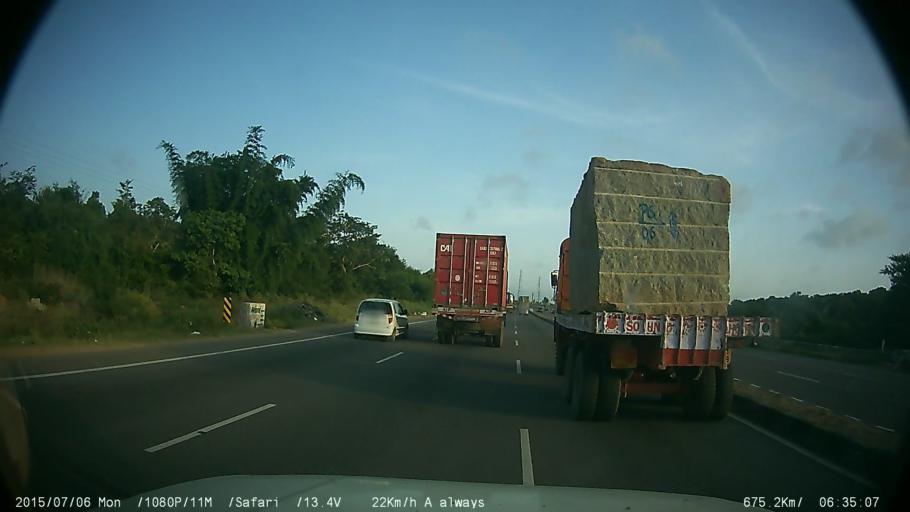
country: IN
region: Tamil Nadu
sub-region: Krishnagiri
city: Hosur
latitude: 12.7053
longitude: 77.9035
